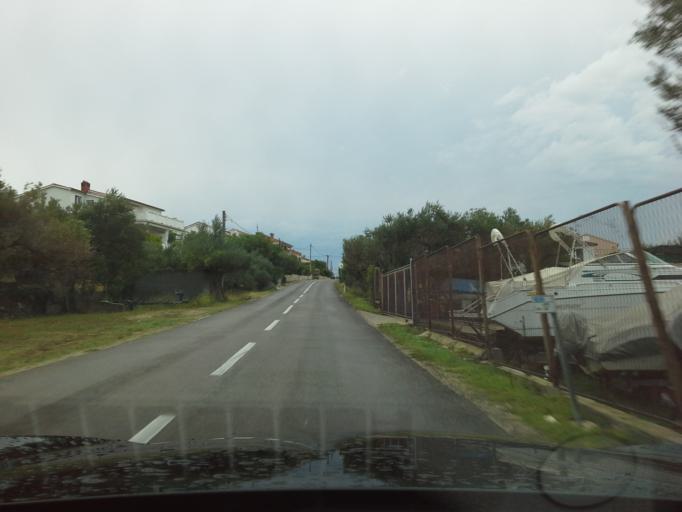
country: HR
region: Primorsko-Goranska
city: Banjol
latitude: 44.7328
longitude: 14.8103
